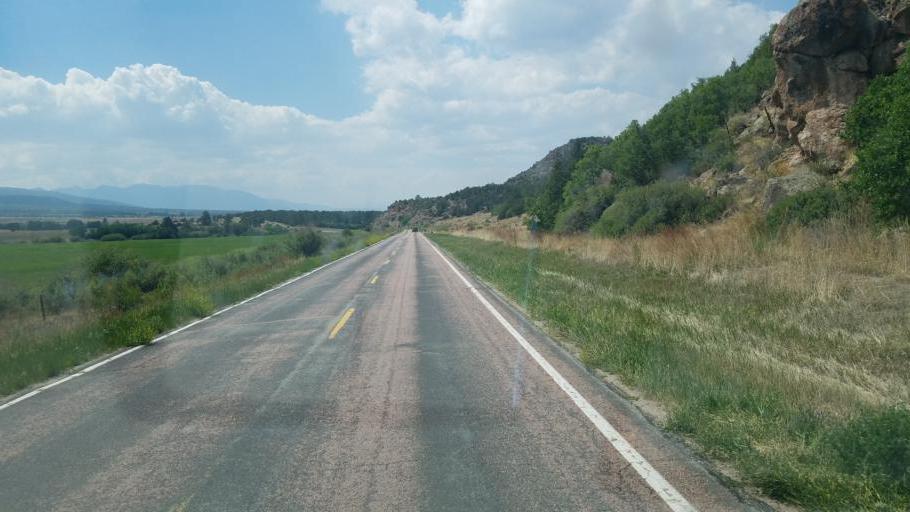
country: US
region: Colorado
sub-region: Custer County
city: Westcliffe
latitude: 38.2596
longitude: -105.5943
